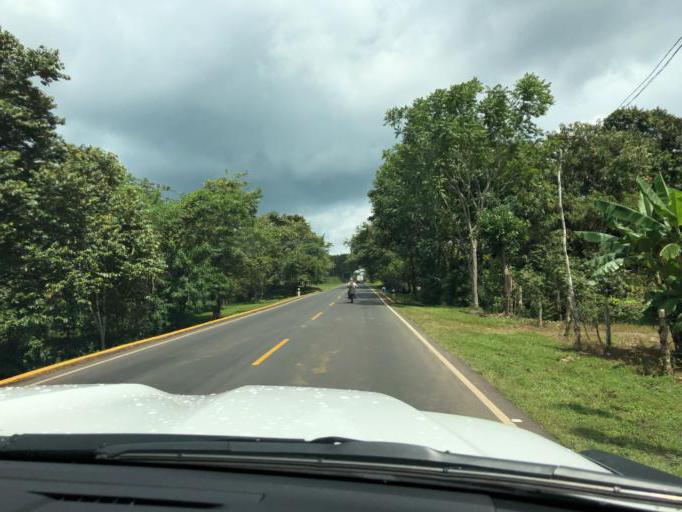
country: NI
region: Chontales
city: Villa Sandino
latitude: 11.9981
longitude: -84.8402
